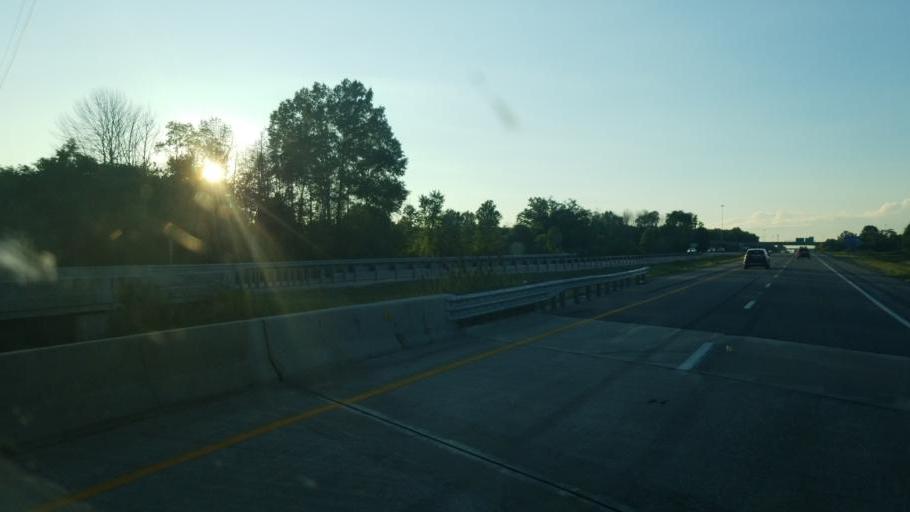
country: US
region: Ohio
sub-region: Mahoning County
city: Austintown
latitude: 41.1005
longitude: -80.8301
